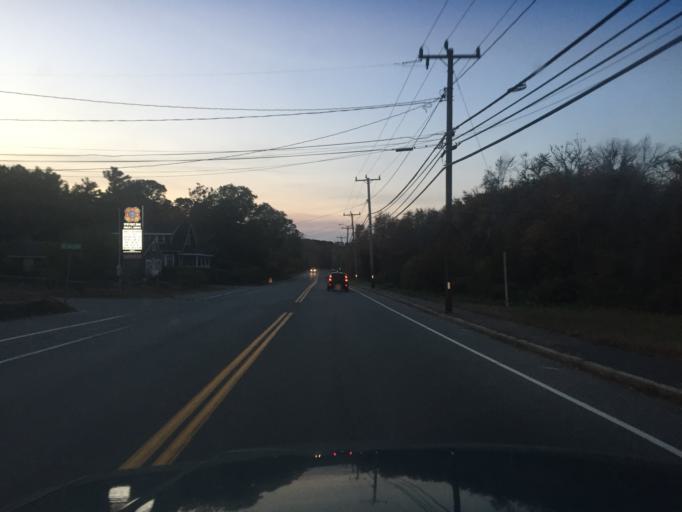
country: US
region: Massachusetts
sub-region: Plymouth County
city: Onset
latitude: 41.7523
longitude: -70.6722
